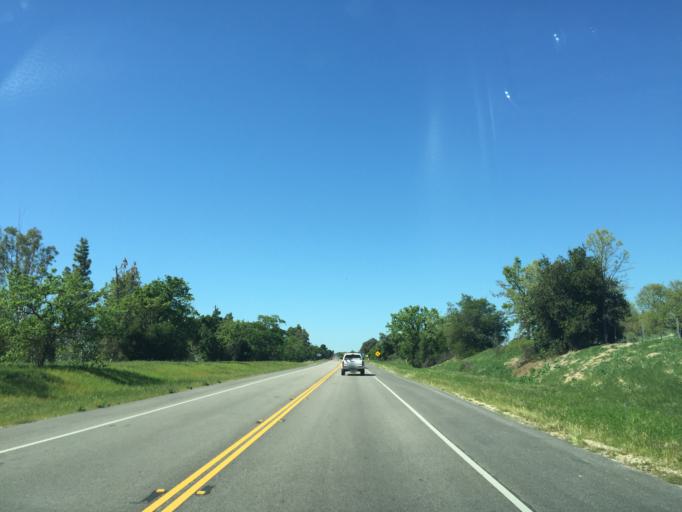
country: US
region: California
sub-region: Santa Barbara County
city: Los Olivos
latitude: 34.6549
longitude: -120.0990
